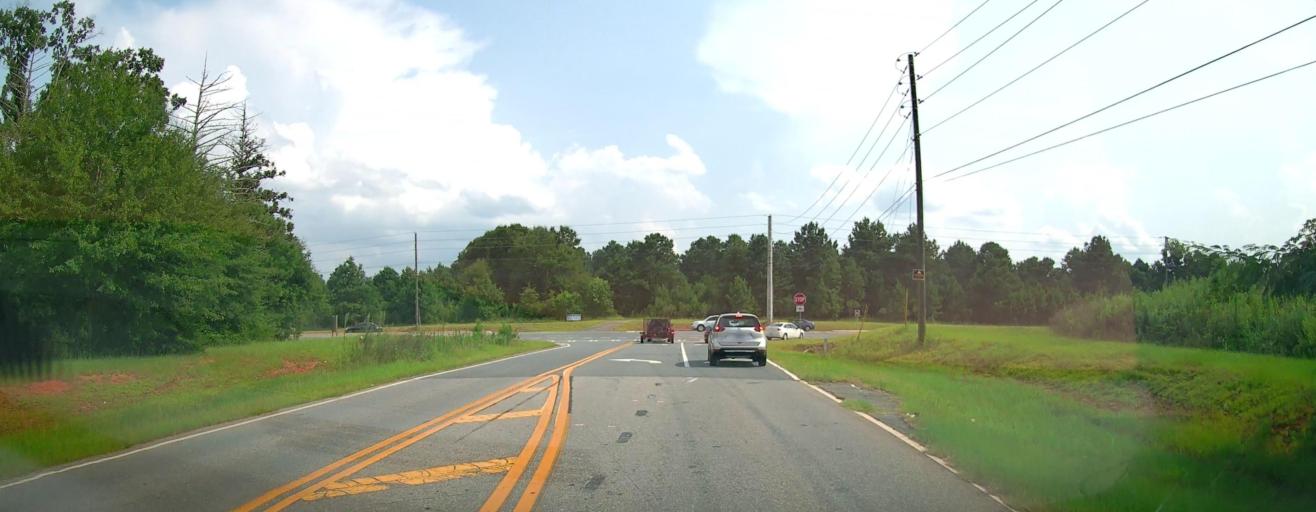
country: US
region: Georgia
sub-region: Houston County
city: Centerville
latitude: 32.5552
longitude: -83.6521
